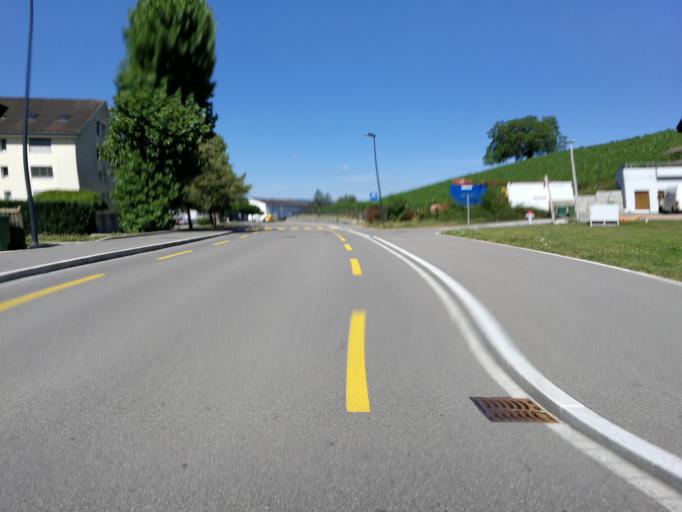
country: CH
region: Zurich
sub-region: Bezirk Uster
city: Uster / Nossikon
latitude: 47.3424
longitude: 8.7232
